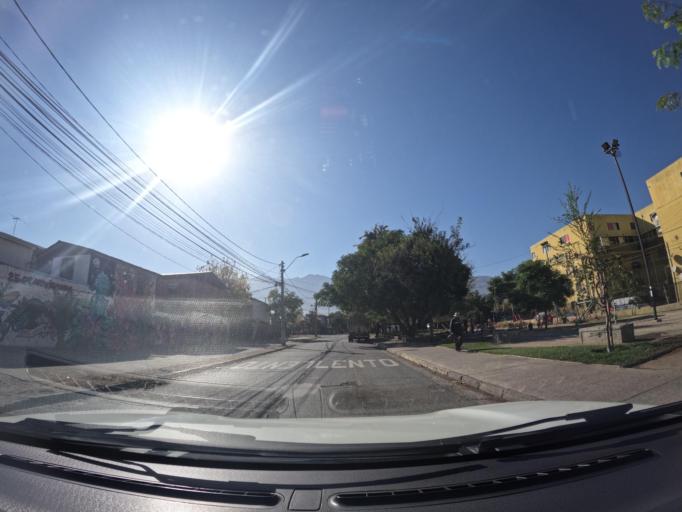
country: CL
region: Santiago Metropolitan
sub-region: Provincia de Santiago
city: Villa Presidente Frei, Nunoa, Santiago, Chile
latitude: -33.5083
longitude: -70.5763
